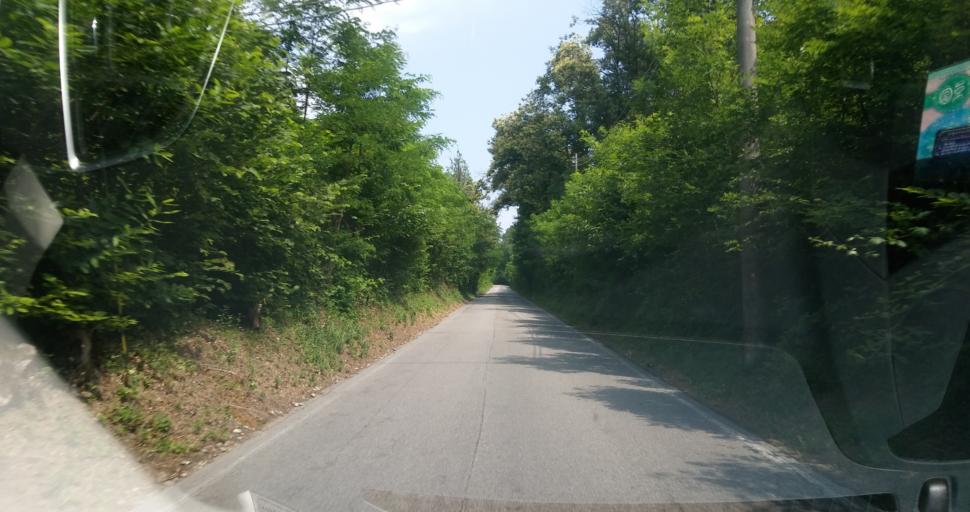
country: IT
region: Lombardy
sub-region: Provincia di Varese
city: Osmate
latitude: 45.7785
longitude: 8.6547
